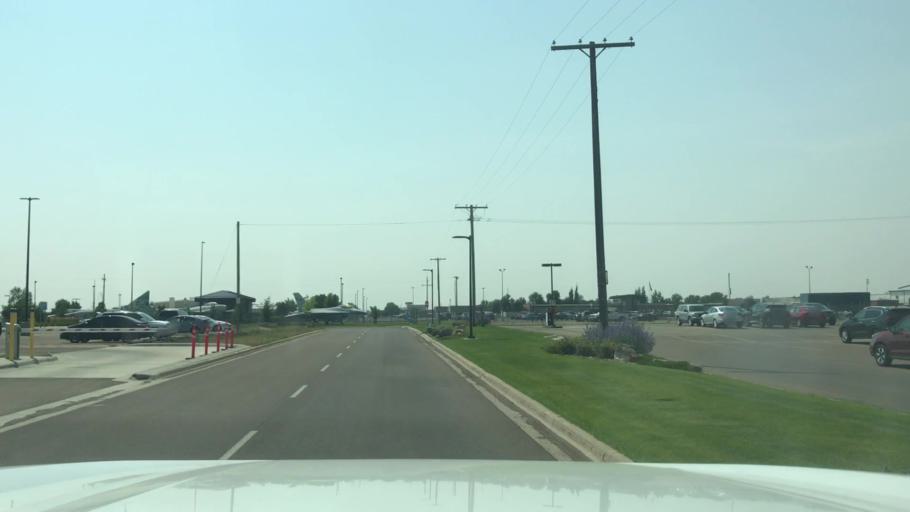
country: US
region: Montana
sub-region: Cascade County
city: Great Falls
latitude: 47.4795
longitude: -111.3585
